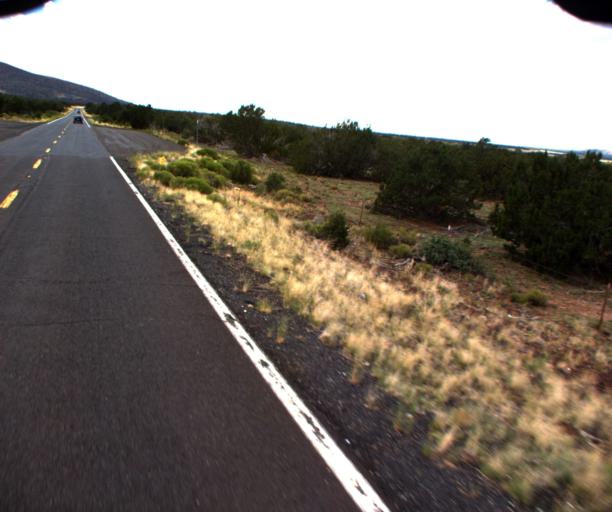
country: US
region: Arizona
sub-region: Coconino County
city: Parks
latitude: 35.5641
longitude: -111.8964
